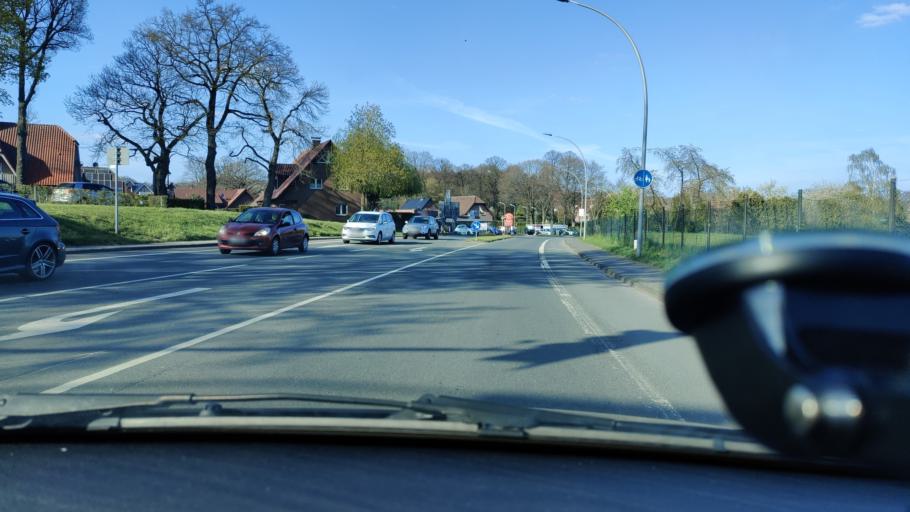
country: DE
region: North Rhine-Westphalia
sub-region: Regierungsbezirk Munster
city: Klein Reken
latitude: 51.8319
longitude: 7.0476
